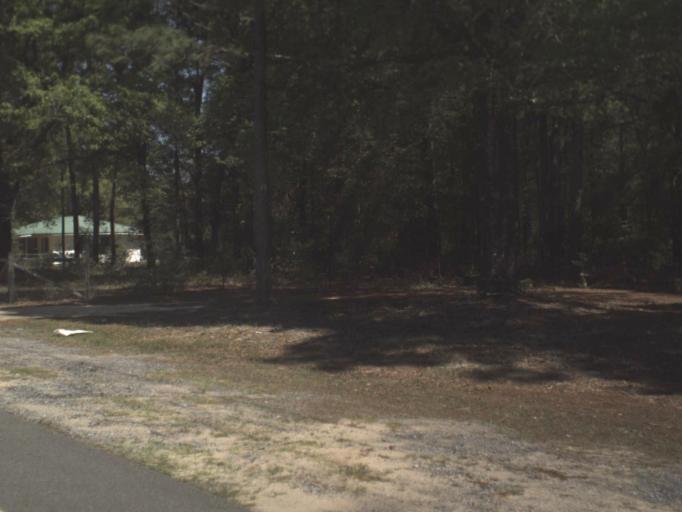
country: US
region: Florida
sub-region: Okaloosa County
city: Crestview
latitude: 30.7068
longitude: -86.7716
